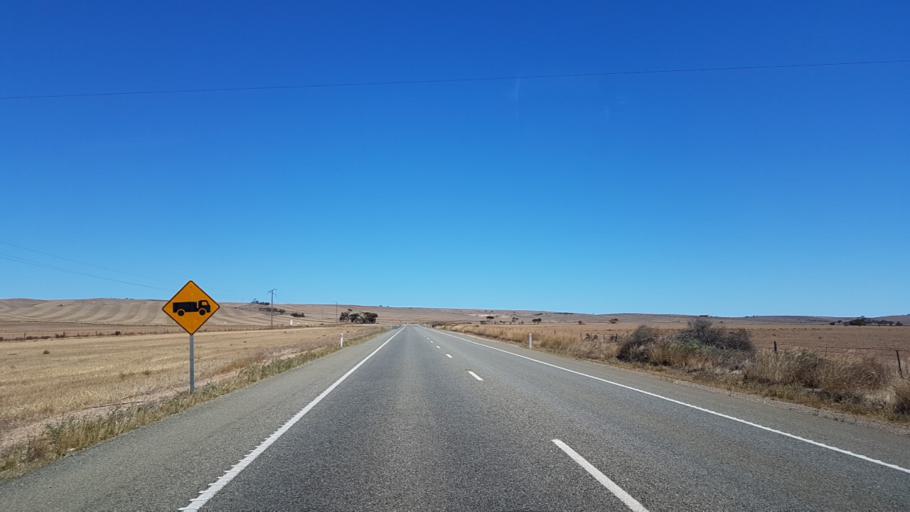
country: AU
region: South Australia
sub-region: Wakefield
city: Balaklava
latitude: -34.0753
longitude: 138.0753
